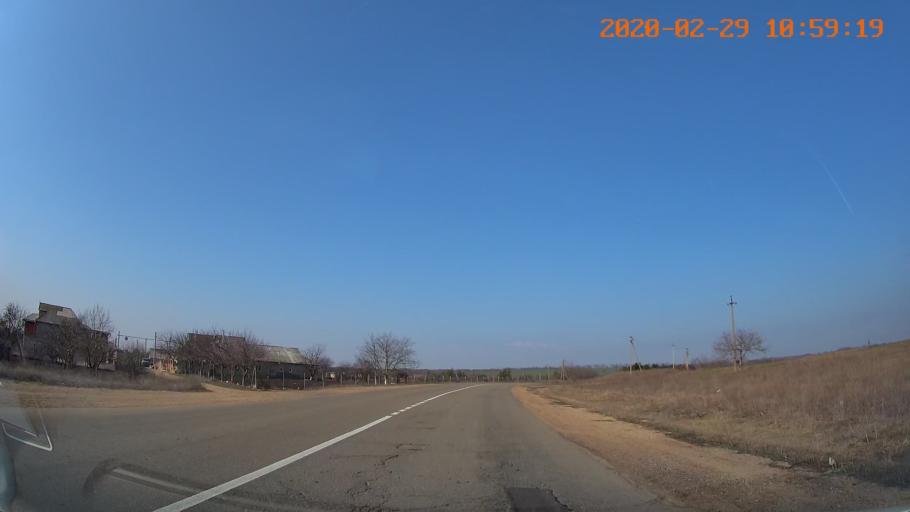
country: MD
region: Telenesti
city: Grigoriopol
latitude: 47.1644
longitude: 29.2938
